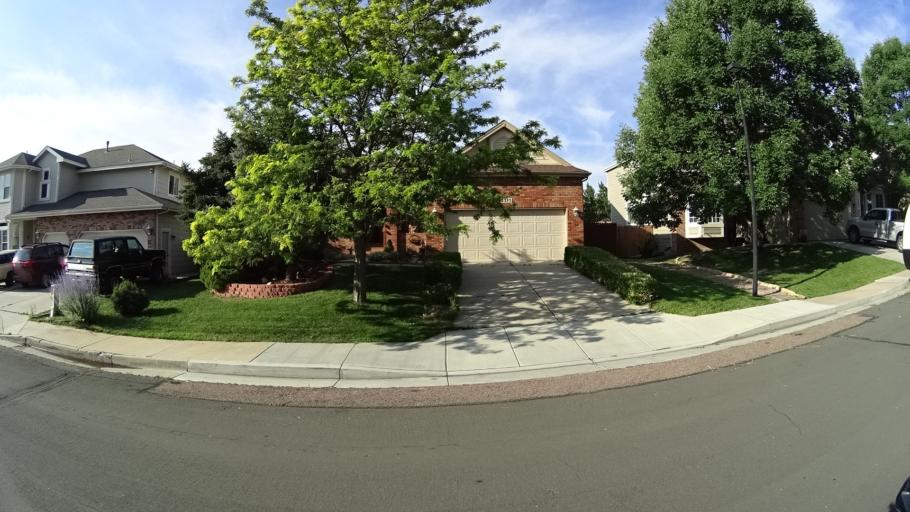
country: US
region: Colorado
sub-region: El Paso County
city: Air Force Academy
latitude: 38.9244
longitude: -104.8498
